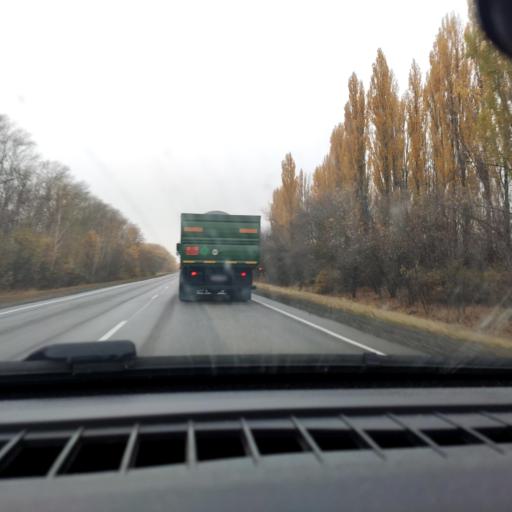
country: RU
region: Voronezj
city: Ostrogozhsk
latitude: 50.9646
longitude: 39.0156
